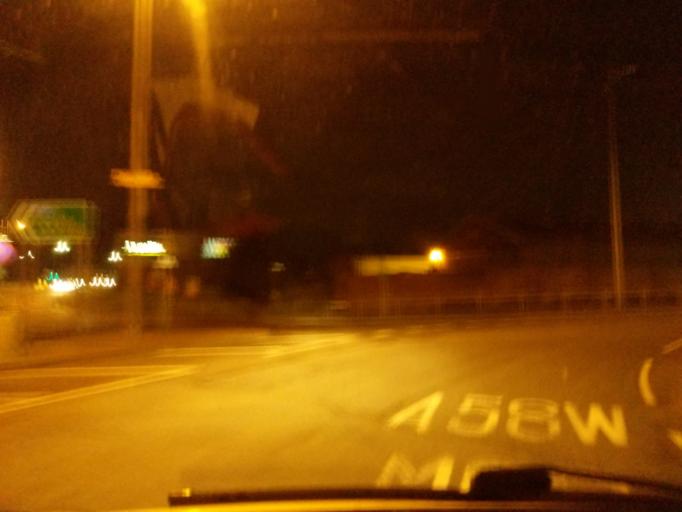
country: GB
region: England
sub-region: St. Helens
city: St Helens
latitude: 53.4521
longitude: -2.7275
